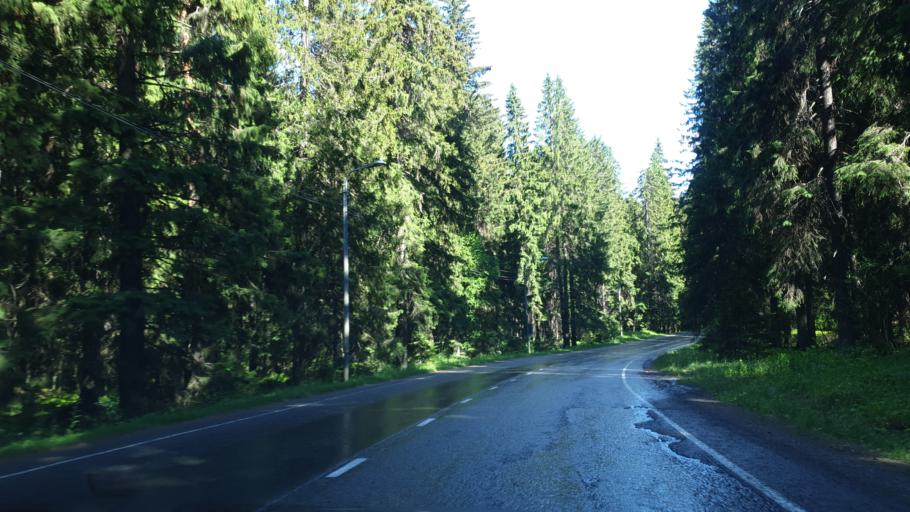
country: FI
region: Northern Savo
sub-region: Kuopio
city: Kuopio
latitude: 62.9084
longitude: 27.6668
